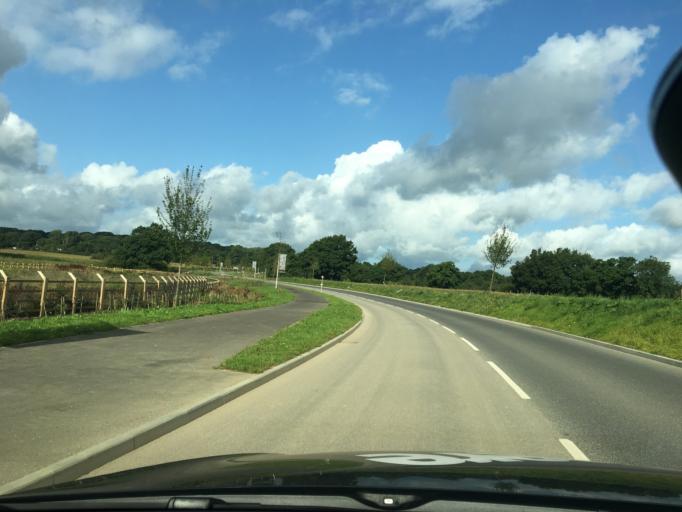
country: GB
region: England
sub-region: Surrey
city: Salfords
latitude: 51.1886
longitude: -0.1867
